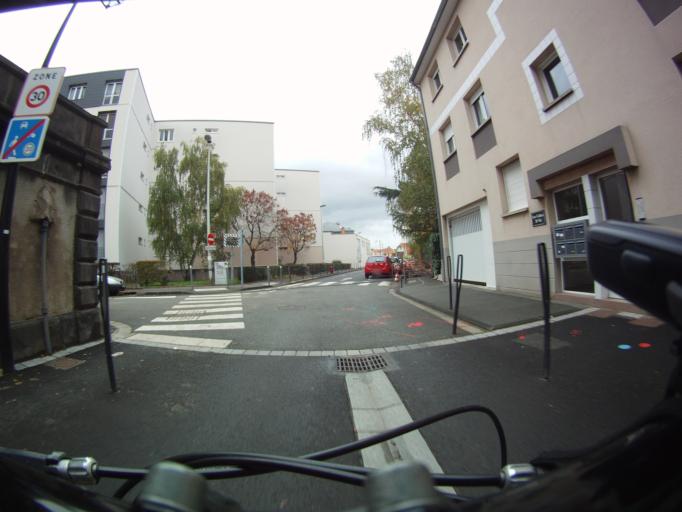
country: FR
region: Auvergne
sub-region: Departement du Puy-de-Dome
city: Beaumont
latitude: 45.7519
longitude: 3.0870
